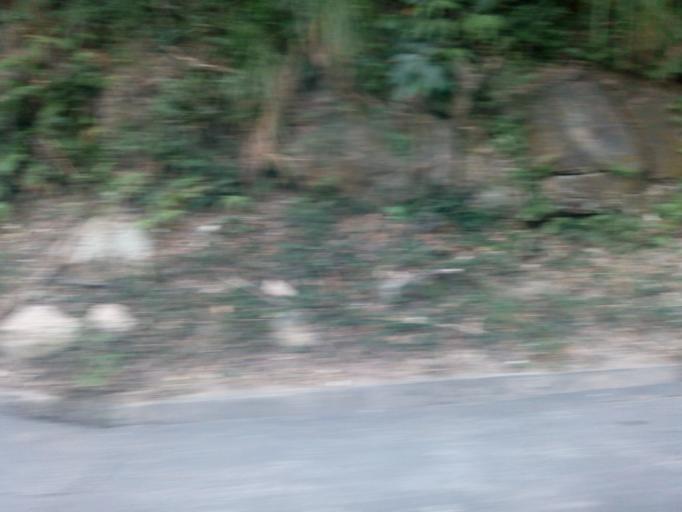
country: MO
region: Macau
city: Macau
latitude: 22.1145
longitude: 113.5578
